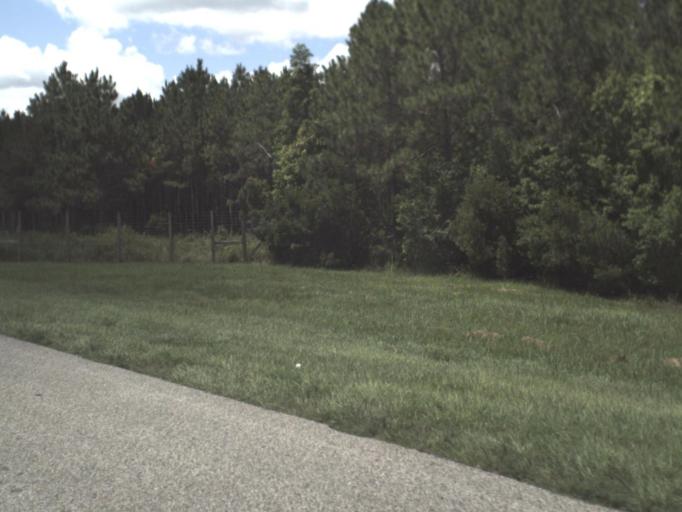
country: US
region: Florida
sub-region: Saint Johns County
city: Saint Augustine Shores
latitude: 29.7609
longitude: -81.3519
